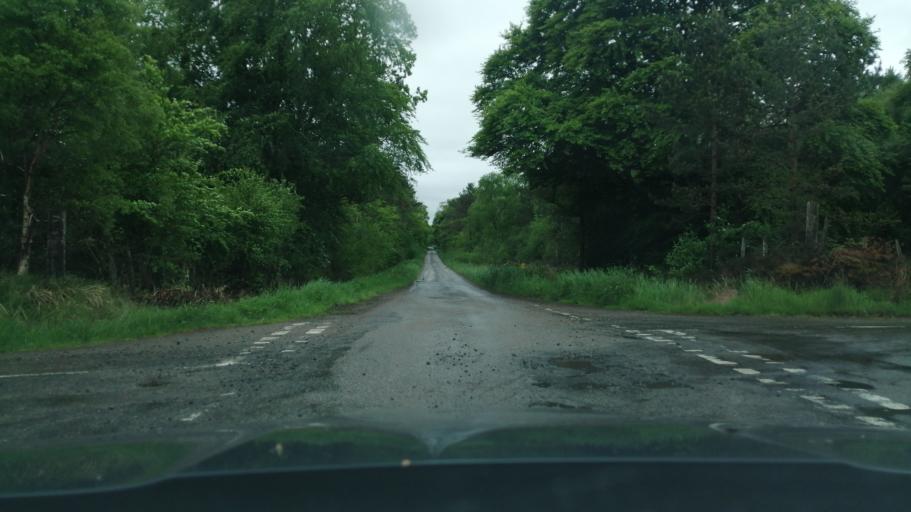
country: GB
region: Scotland
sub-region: Moray
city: Cullen
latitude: 57.5738
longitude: -2.8282
